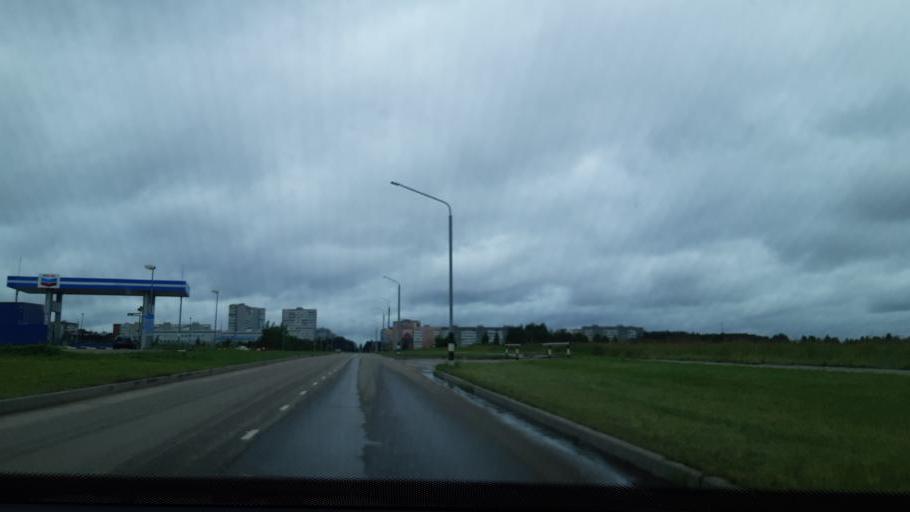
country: RU
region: Smolensk
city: Desnogorsk
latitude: 54.1415
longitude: 33.2789
